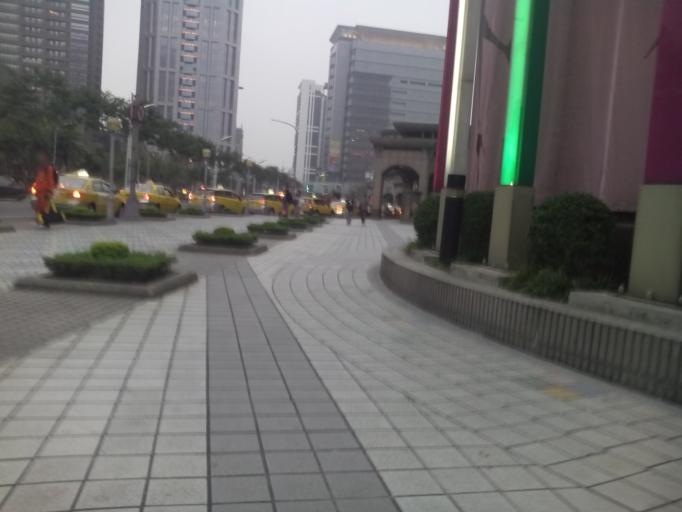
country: TW
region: Taipei
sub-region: Taipei
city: Banqiao
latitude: 25.0145
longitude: 121.4649
